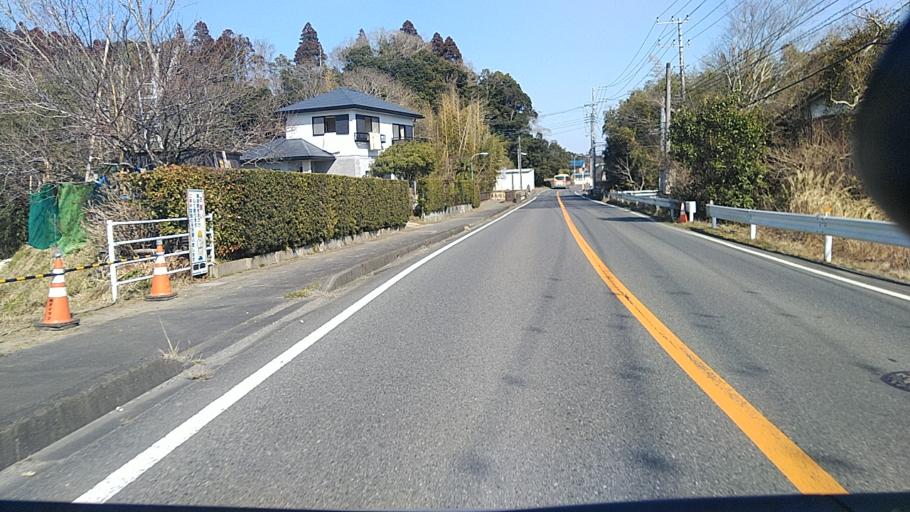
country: JP
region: Chiba
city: Mobara
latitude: 35.4093
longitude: 140.2421
